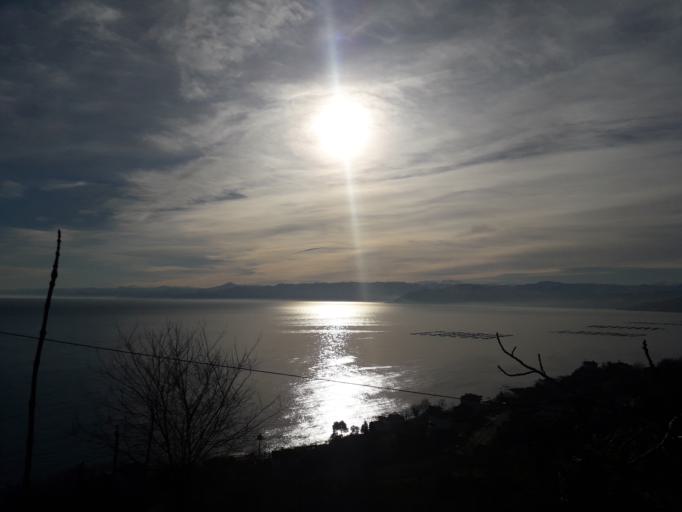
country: TR
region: Ordu
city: Persembe
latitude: 41.1089
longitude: 37.7864
